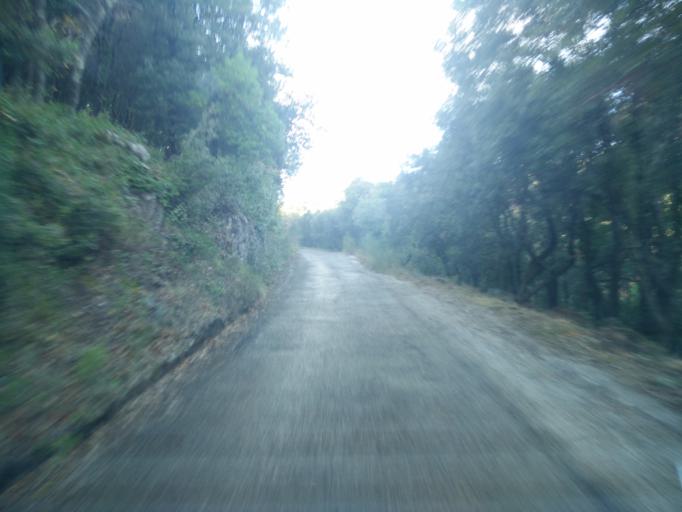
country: FR
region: Provence-Alpes-Cote d'Azur
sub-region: Departement du Var
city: Belgentier
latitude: 43.2102
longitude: 5.9692
